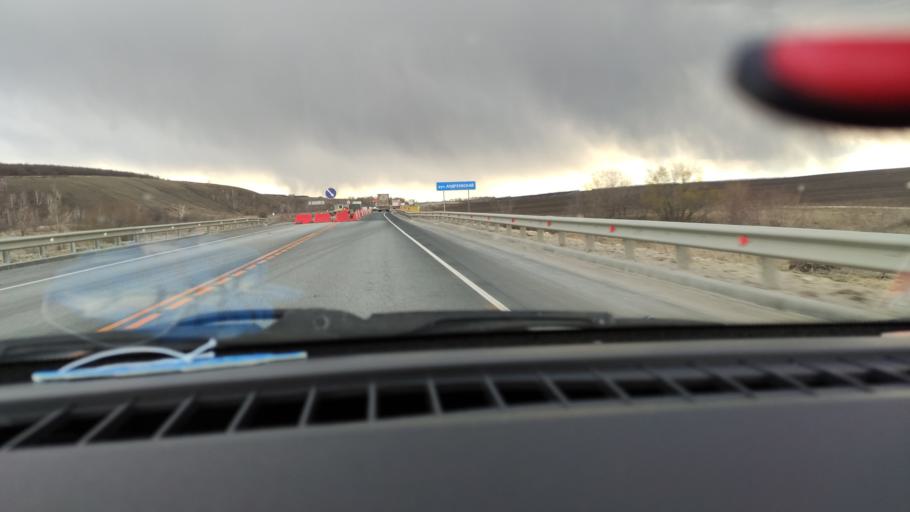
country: RU
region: Saratov
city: Yelshanka
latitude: 51.8634
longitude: 46.5003
